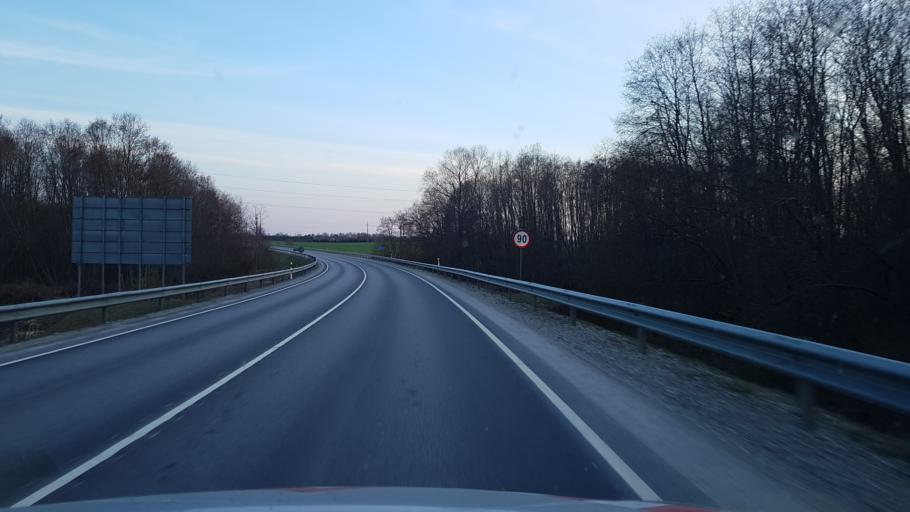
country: EE
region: Laeaene-Virumaa
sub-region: Kadrina vald
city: Kadrina
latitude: 59.3443
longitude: 26.1232
